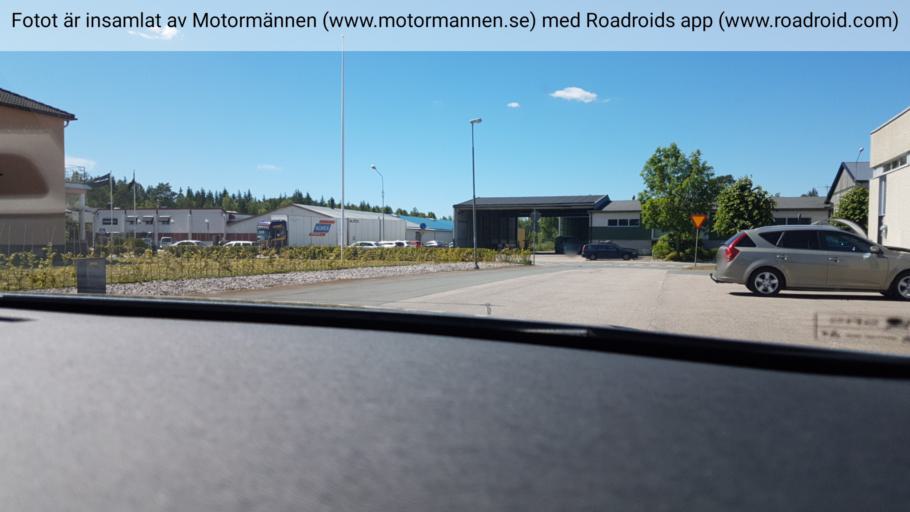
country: SE
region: Joenkoeping
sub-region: Gnosjo Kommun
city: Hillerstorp
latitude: 57.3107
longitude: 13.8785
